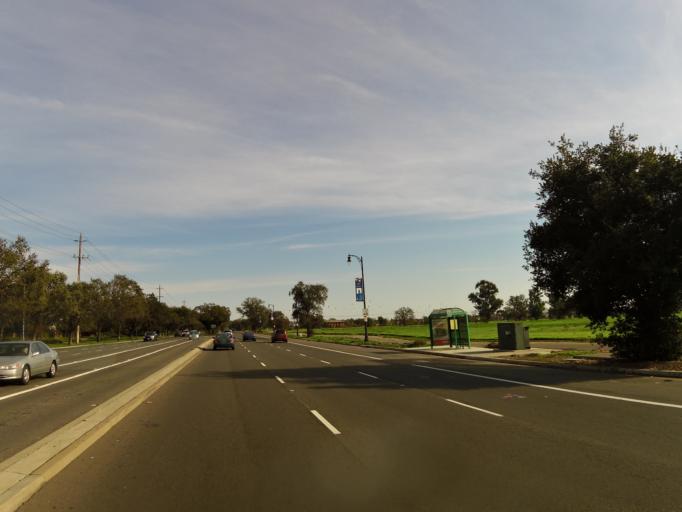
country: US
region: California
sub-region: Sacramento County
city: Laguna
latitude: 38.4090
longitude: -121.4050
